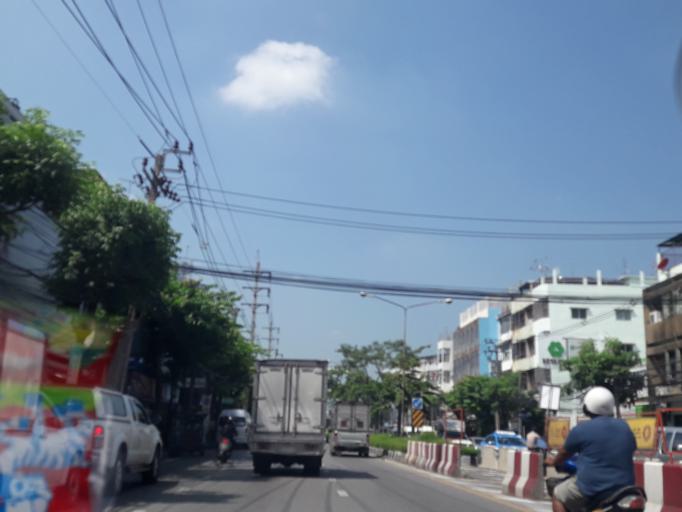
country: TH
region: Bangkok
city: Bangkok Noi
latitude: 13.7549
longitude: 100.4717
